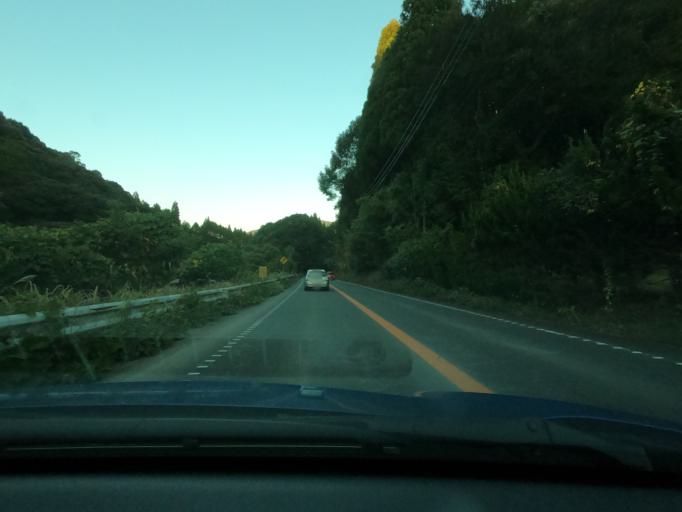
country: JP
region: Kagoshima
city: Satsumasendai
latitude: 31.7968
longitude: 130.4246
